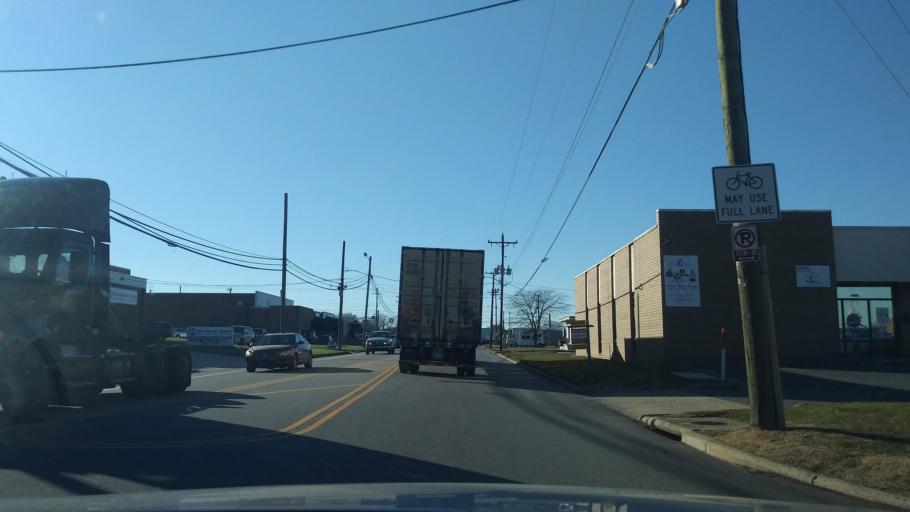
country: US
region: North Carolina
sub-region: Guilford County
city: Greensboro
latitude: 36.0292
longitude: -79.7894
